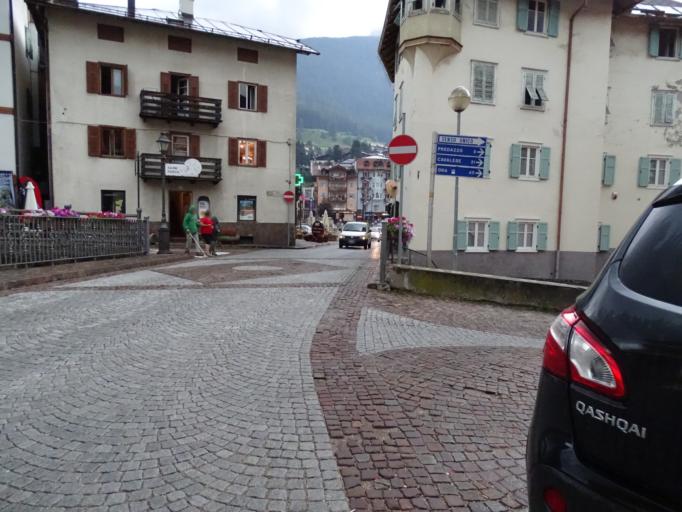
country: IT
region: Trentino-Alto Adige
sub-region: Provincia di Trento
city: Moena
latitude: 46.3667
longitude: 11.6500
